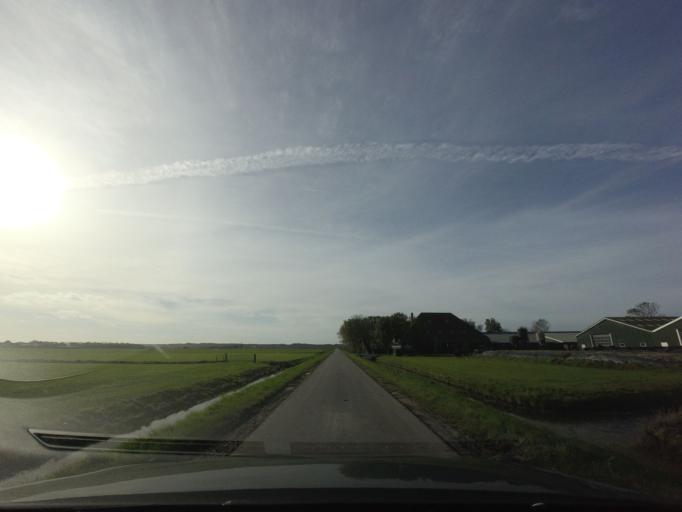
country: NL
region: North Holland
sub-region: Gemeente Schagen
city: Harenkarspel
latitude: 52.7436
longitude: 4.6815
